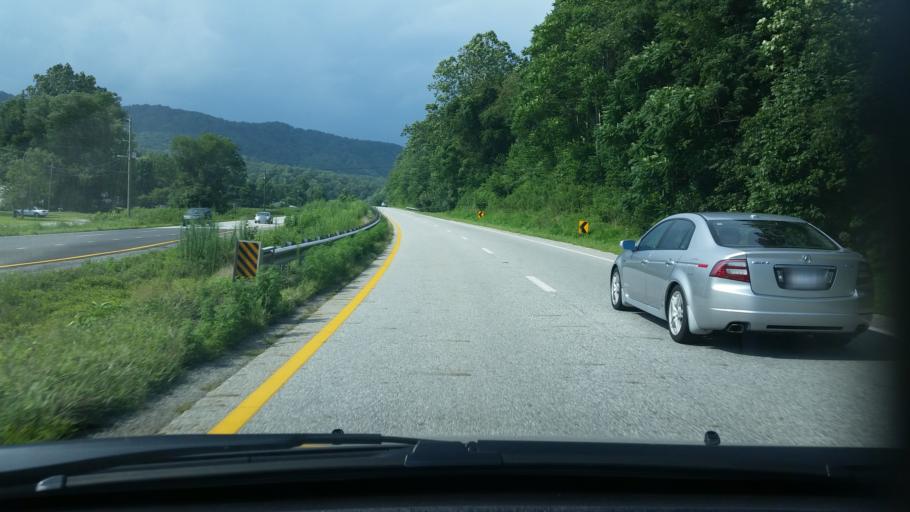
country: US
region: Virginia
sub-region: Nelson County
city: Lovingston
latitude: 37.7967
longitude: -78.8620
